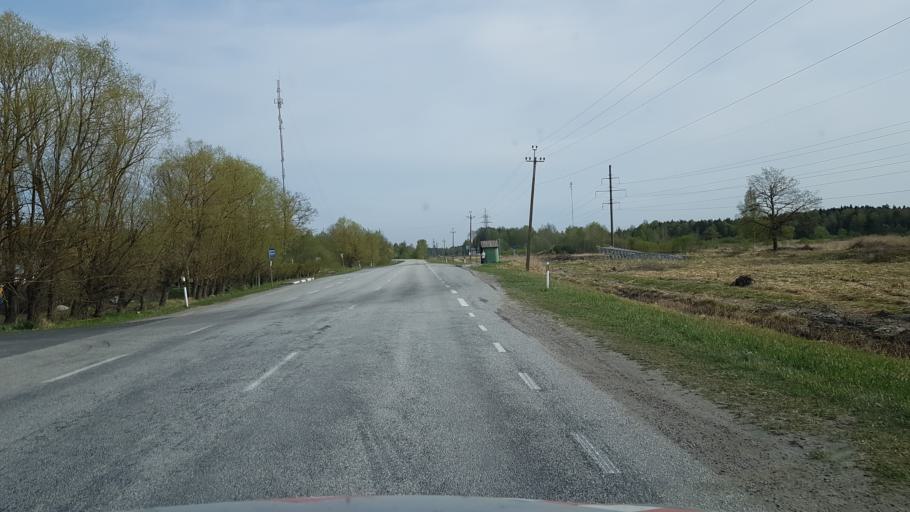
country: EE
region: Paernumaa
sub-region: Audru vald
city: Audru
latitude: 58.4129
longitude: 24.3100
